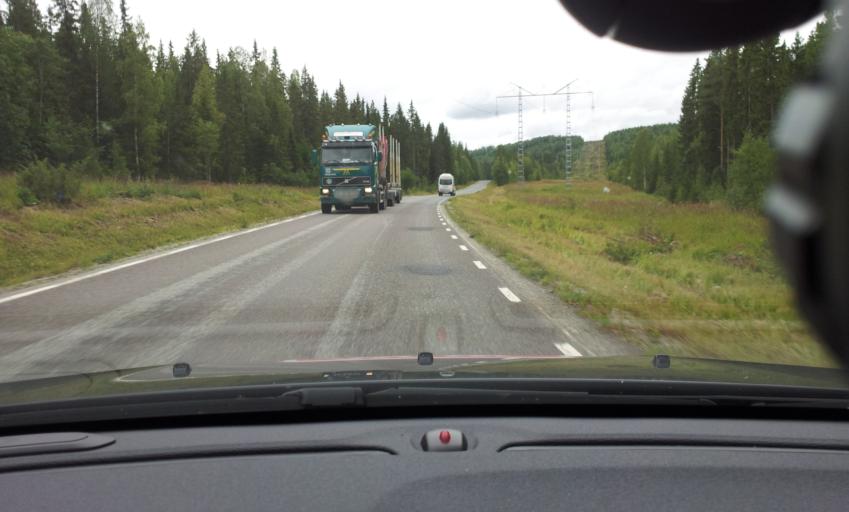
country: SE
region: Jaemtland
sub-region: Braecke Kommun
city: Braecke
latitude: 63.0038
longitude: 15.1982
